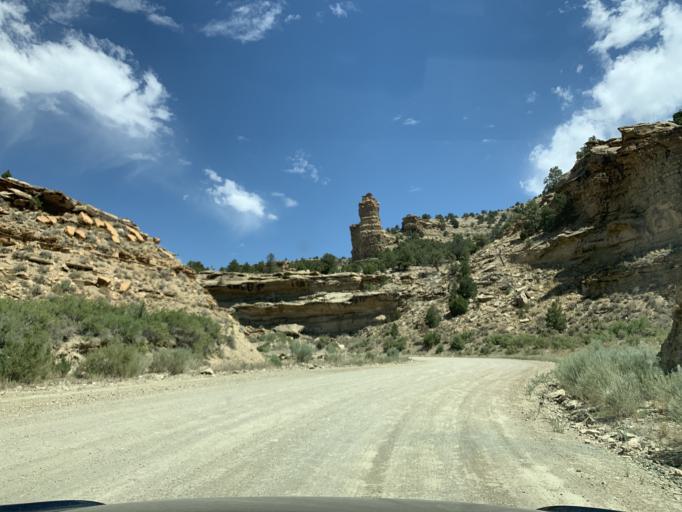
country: US
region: Utah
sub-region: Carbon County
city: East Carbon City
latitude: 39.8245
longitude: -110.2482
